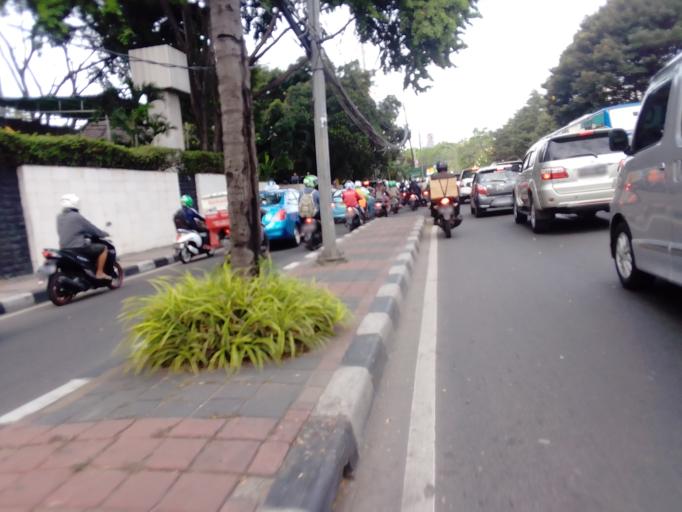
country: ID
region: Jakarta Raya
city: Jakarta
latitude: -6.1820
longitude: 106.8356
